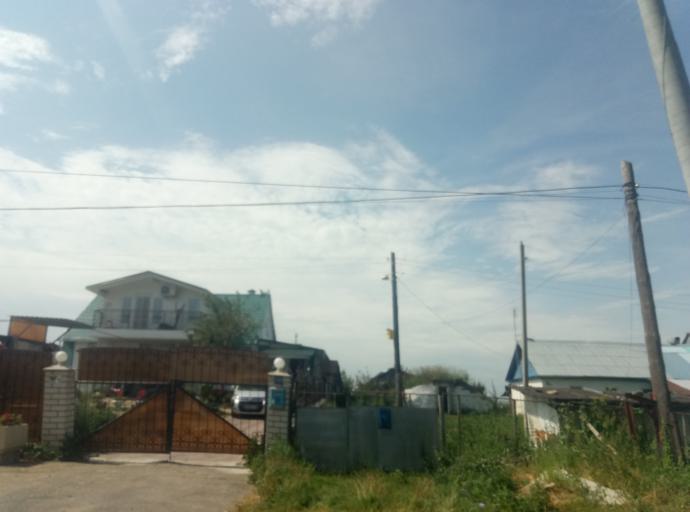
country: RU
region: Tula
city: Dubovka
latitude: 53.9005
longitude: 38.0358
